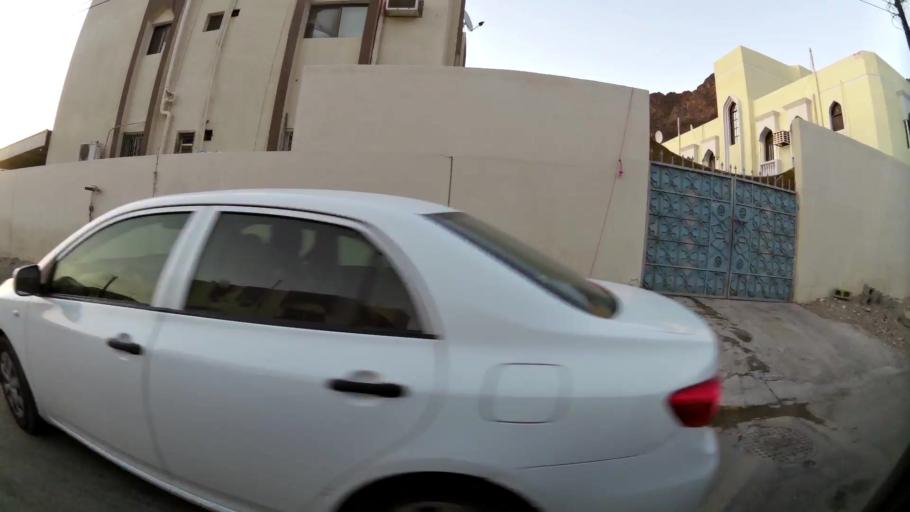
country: OM
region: Muhafazat Masqat
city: Muscat
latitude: 23.5834
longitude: 58.5684
